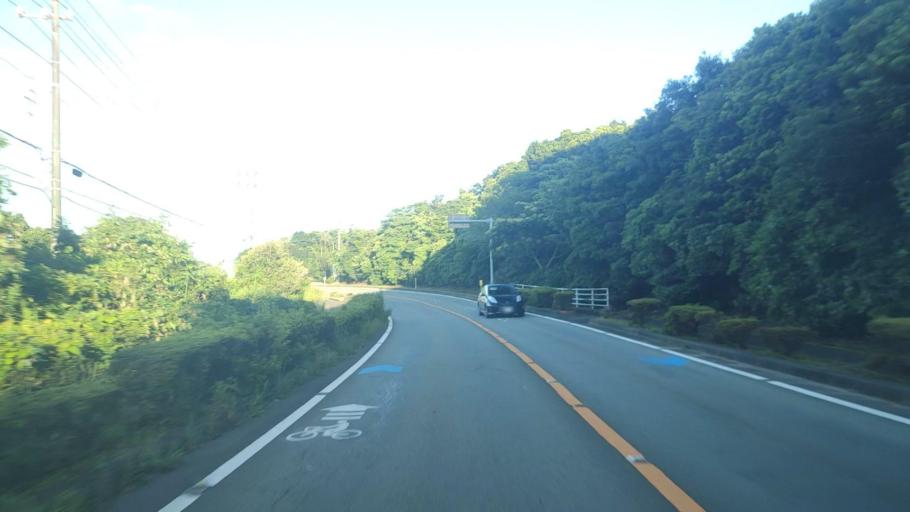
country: JP
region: Mie
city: Toba
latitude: 34.2629
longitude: 136.8597
